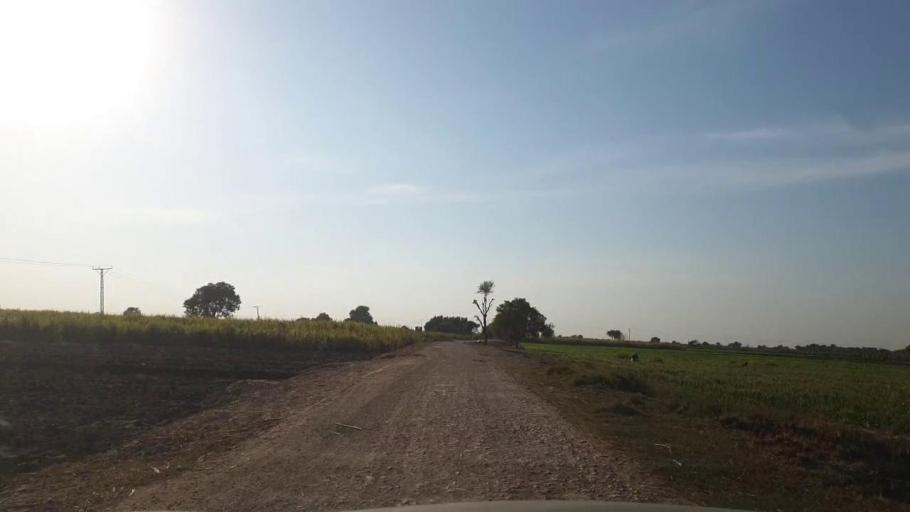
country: PK
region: Sindh
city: Tando Adam
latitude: 25.6942
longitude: 68.7161
